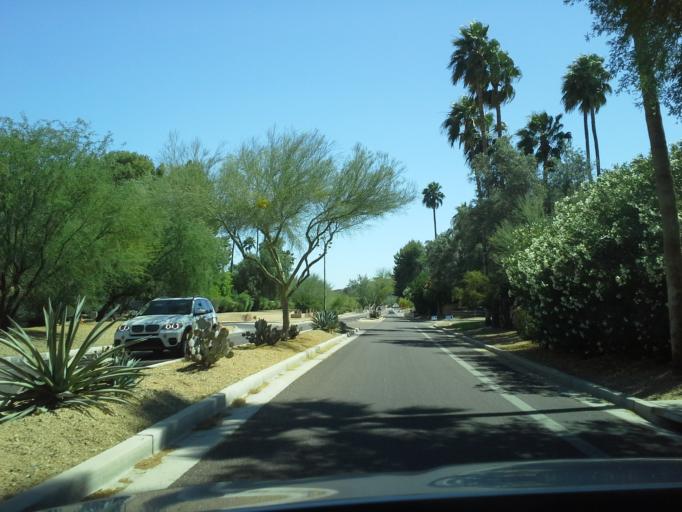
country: US
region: Arizona
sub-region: Maricopa County
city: Paradise Valley
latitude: 33.5653
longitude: -111.9435
